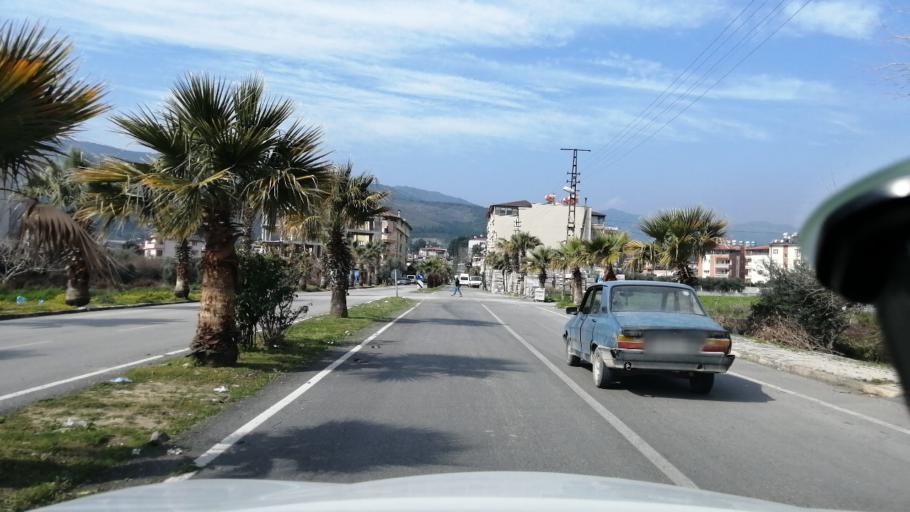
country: TR
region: Hatay
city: Serinyol
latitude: 36.3518
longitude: 36.2128
